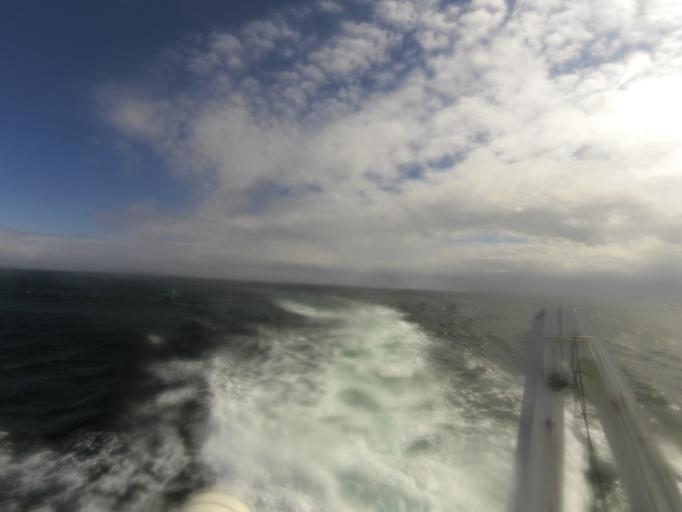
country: IE
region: Connaught
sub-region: County Galway
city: Oughterard
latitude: 53.1215
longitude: -9.6400
